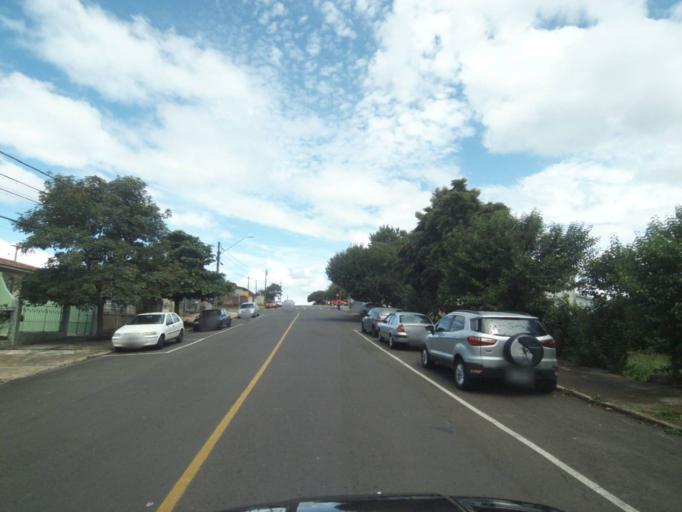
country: BR
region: Parana
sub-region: Telemaco Borba
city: Telemaco Borba
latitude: -24.3204
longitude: -50.6408
